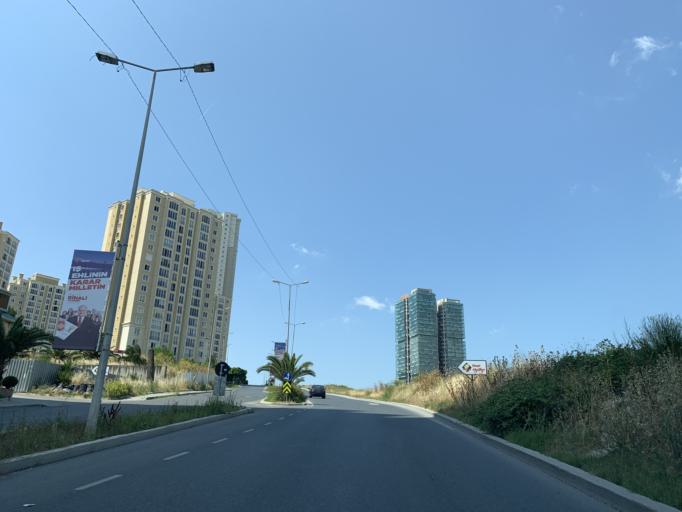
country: TR
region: Istanbul
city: Esenyurt
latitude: 41.0714
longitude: 28.7002
